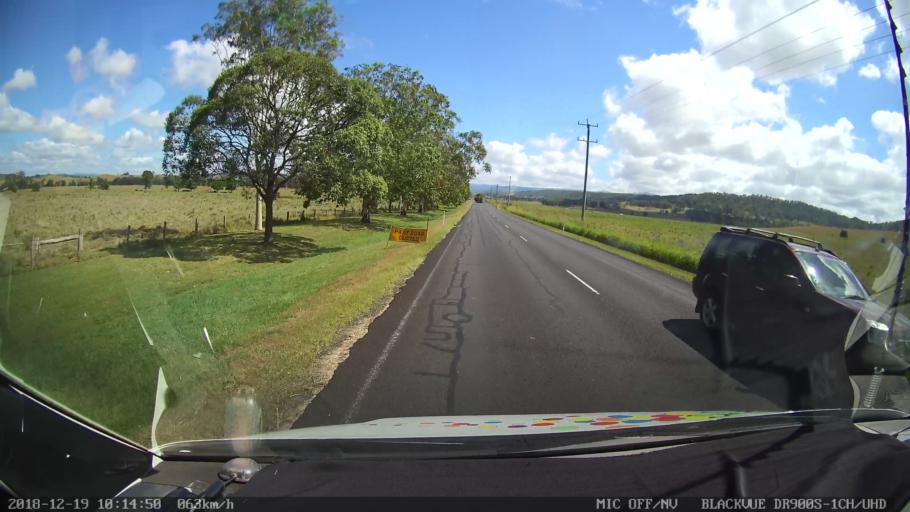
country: AU
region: New South Wales
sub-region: Kyogle
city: Kyogle
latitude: -28.6108
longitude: 153.0100
